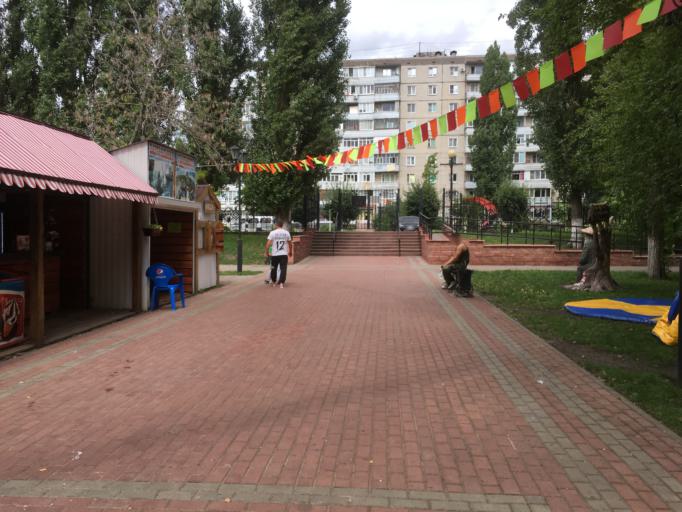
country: RU
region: Voronezj
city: Rossosh'
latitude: 50.1969
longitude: 39.5775
